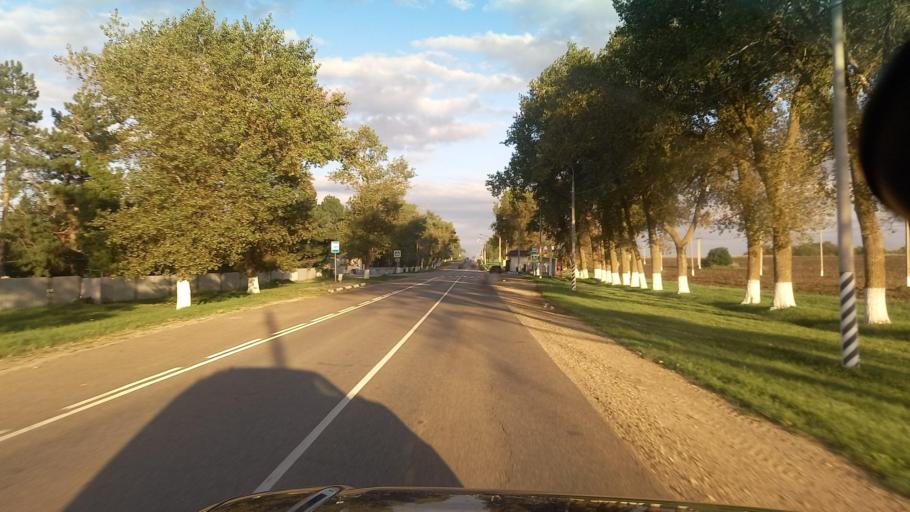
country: RU
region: Krasnodarskiy
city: Krymsk
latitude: 44.9385
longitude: 37.9507
